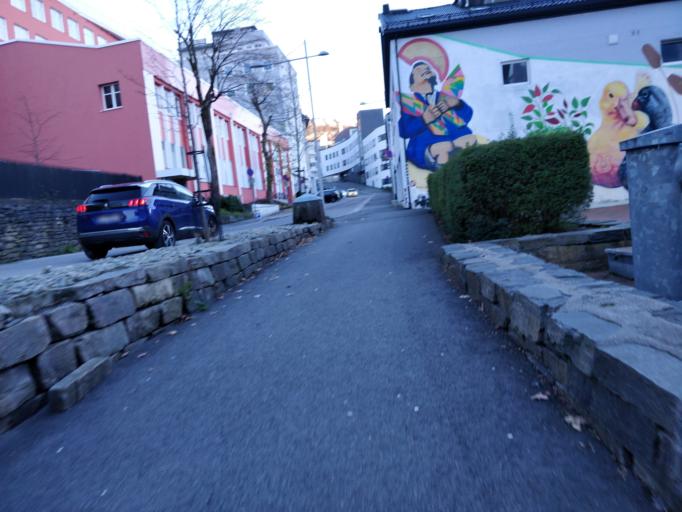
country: NO
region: Hordaland
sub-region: Bergen
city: Bergen
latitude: 60.3790
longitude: 5.3526
